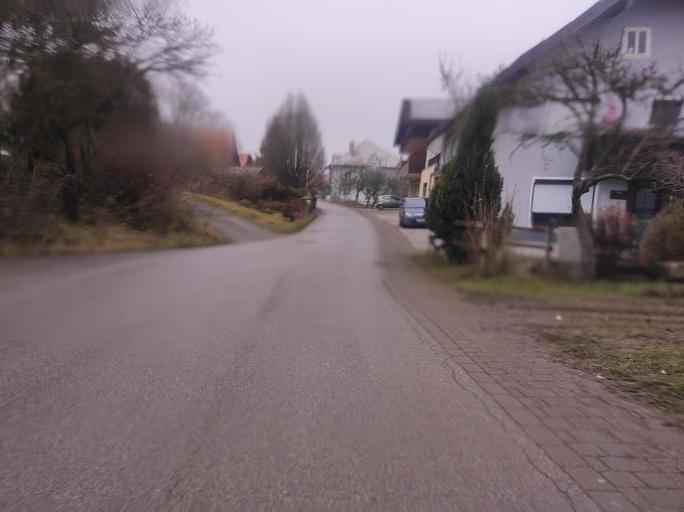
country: AT
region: Salzburg
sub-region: Politischer Bezirk Salzburg-Umgebung
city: Schleedorf
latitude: 47.9546
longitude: 13.1519
